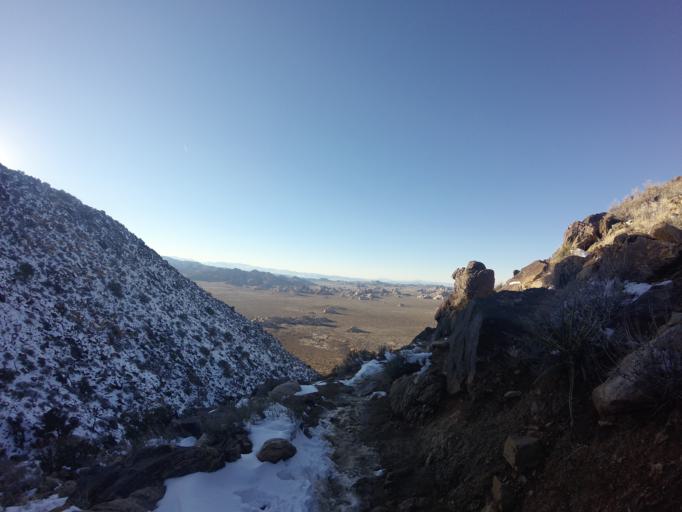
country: US
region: California
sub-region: San Bernardino County
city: Twentynine Palms
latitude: 33.9930
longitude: -116.1350
